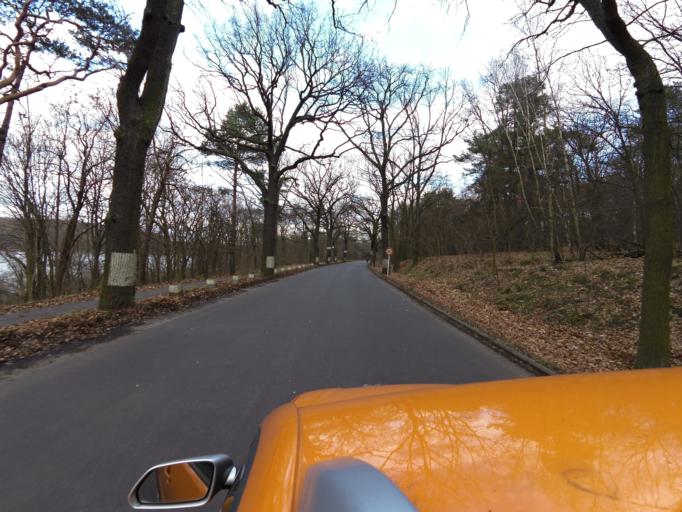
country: DE
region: Berlin
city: Gatow
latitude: 52.4984
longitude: 13.2054
